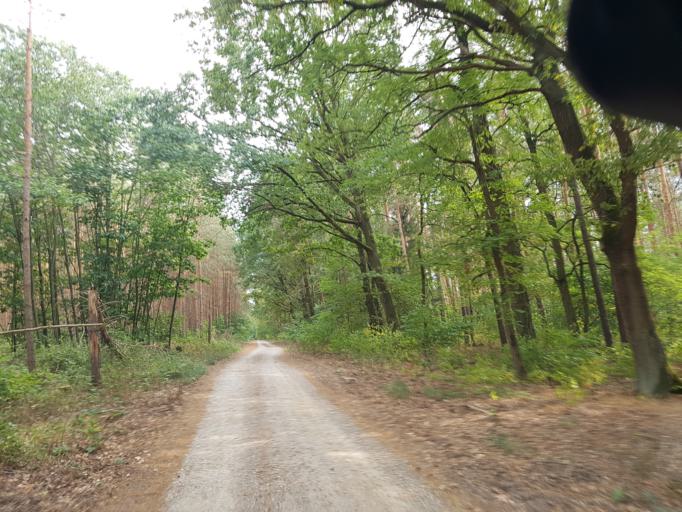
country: DE
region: Saxony-Anhalt
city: Rosslau
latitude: 52.0293
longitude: 12.2868
